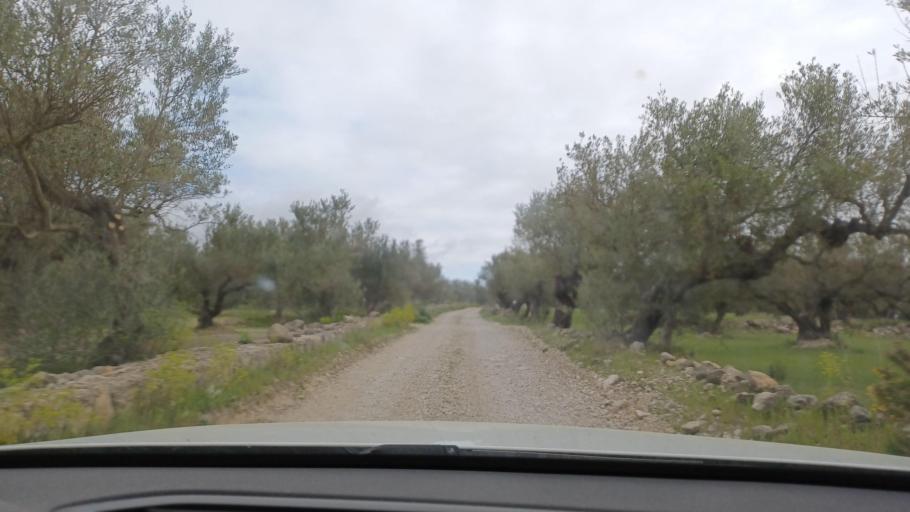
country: ES
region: Catalonia
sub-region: Provincia de Tarragona
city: Mas de Barberans
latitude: 40.8037
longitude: 0.4101
